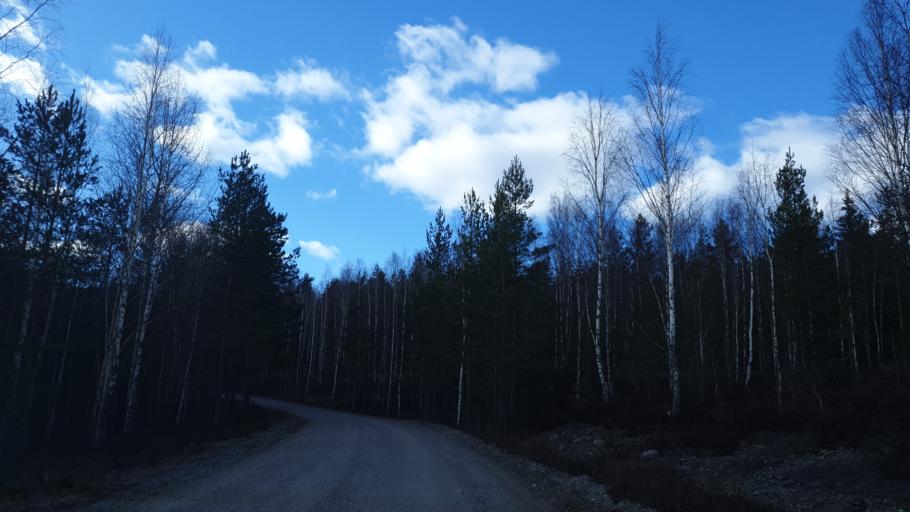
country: SE
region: OErebro
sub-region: Orebro Kommun
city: Garphyttan
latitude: 59.3617
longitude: 14.9779
